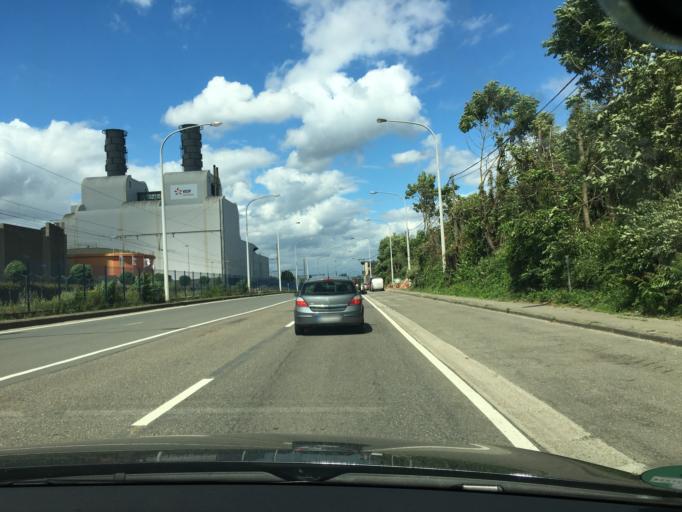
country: BE
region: Wallonia
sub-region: Province de Liege
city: Seraing
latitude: 50.6011
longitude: 5.4899
